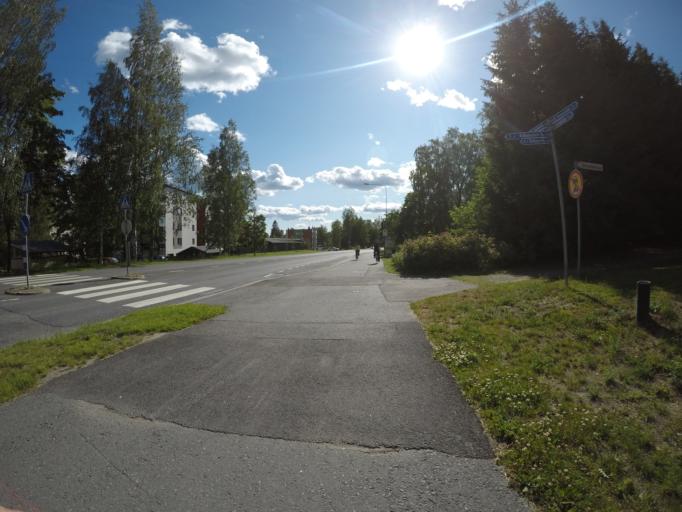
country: FI
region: Haeme
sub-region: Haemeenlinna
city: Haemeenlinna
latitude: 61.0039
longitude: 24.4976
